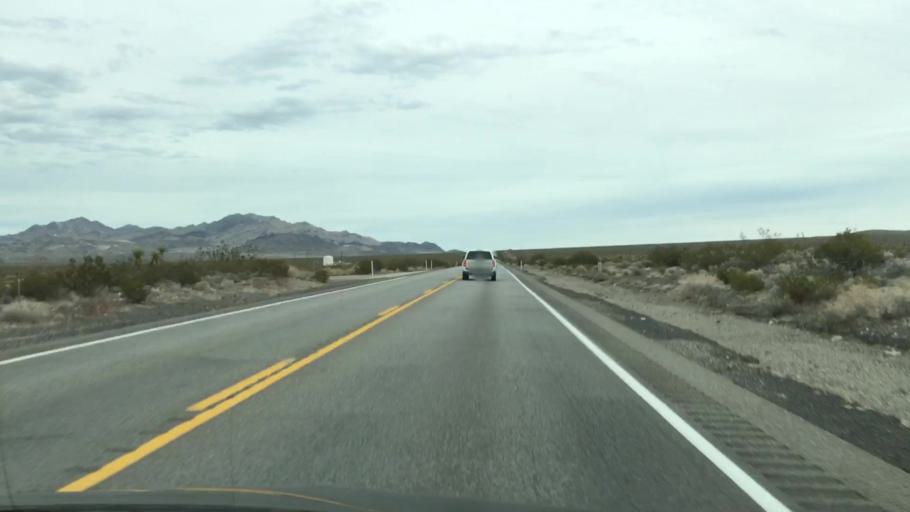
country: US
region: Nevada
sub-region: Nye County
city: Pahrump
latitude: 36.5895
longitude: -116.0447
